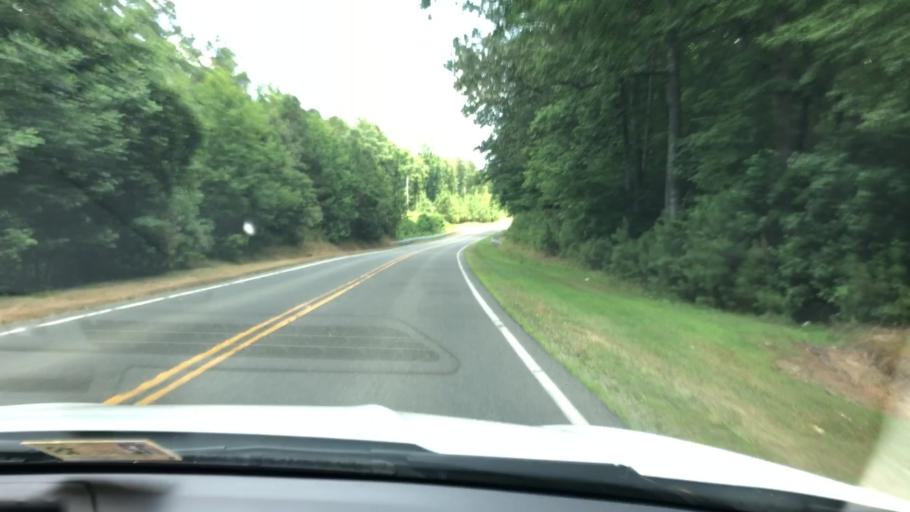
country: US
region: Virginia
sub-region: Lancaster County
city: Lancaster
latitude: 37.8267
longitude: -76.5639
